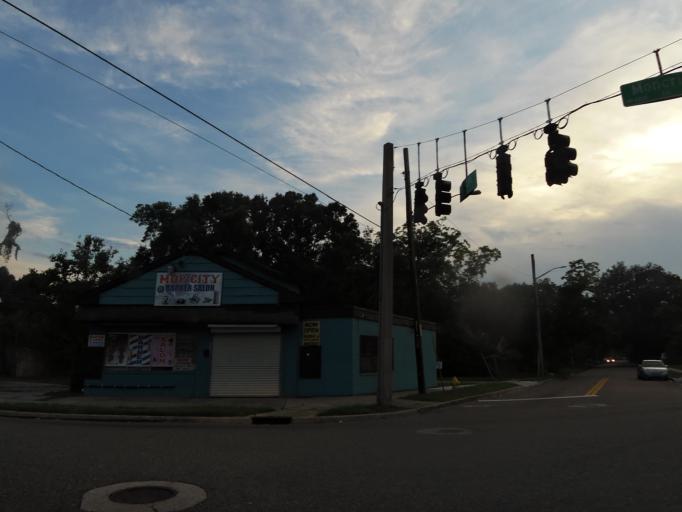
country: US
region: Florida
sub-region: Duval County
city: Jacksonville
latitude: 30.3657
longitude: -81.6800
